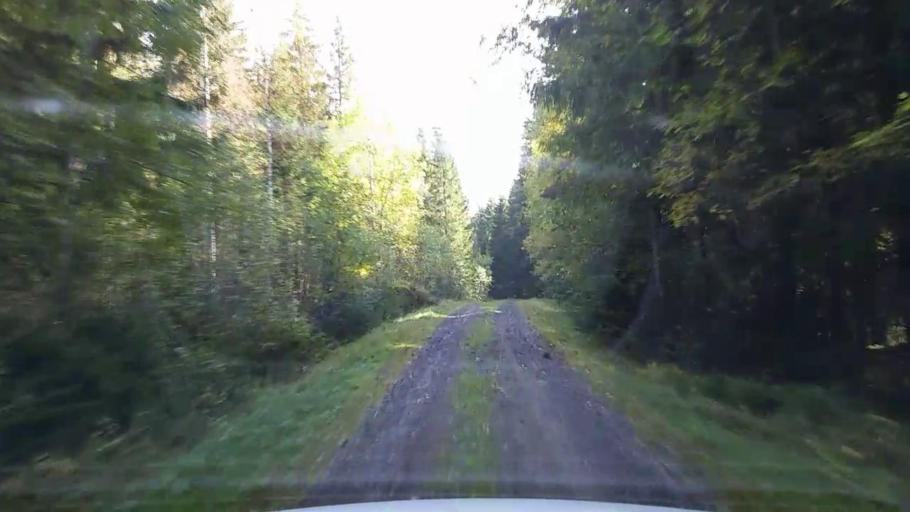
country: SE
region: Gaevleborg
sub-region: Ljusdals Kommun
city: Jaervsoe
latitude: 61.7813
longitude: 16.1763
